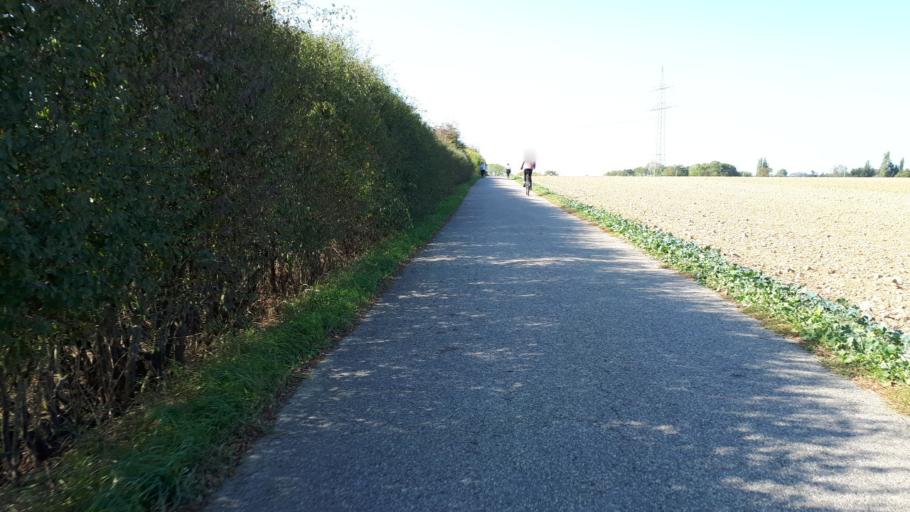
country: LU
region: Luxembourg
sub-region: Canton de Luxembourg
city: Bertrange
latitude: 49.6188
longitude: 6.0441
